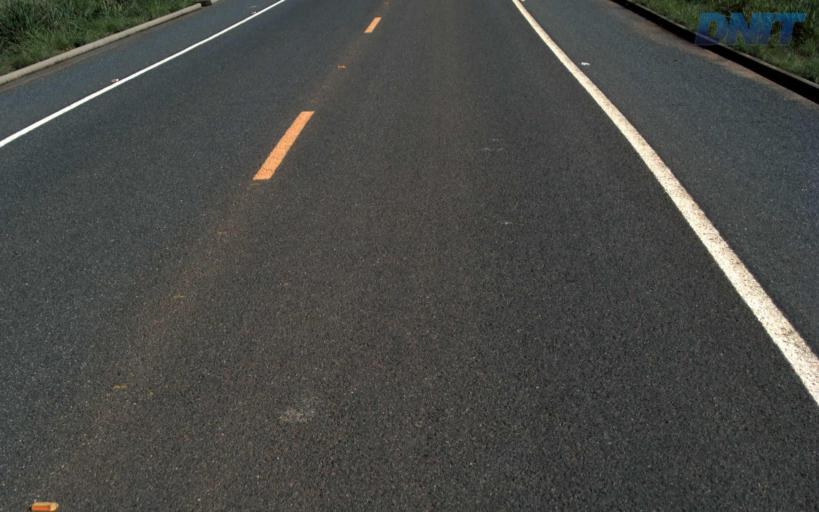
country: BR
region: Goias
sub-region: Sao Miguel Do Araguaia
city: Sao Miguel do Araguaia
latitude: -13.4291
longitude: -50.1269
